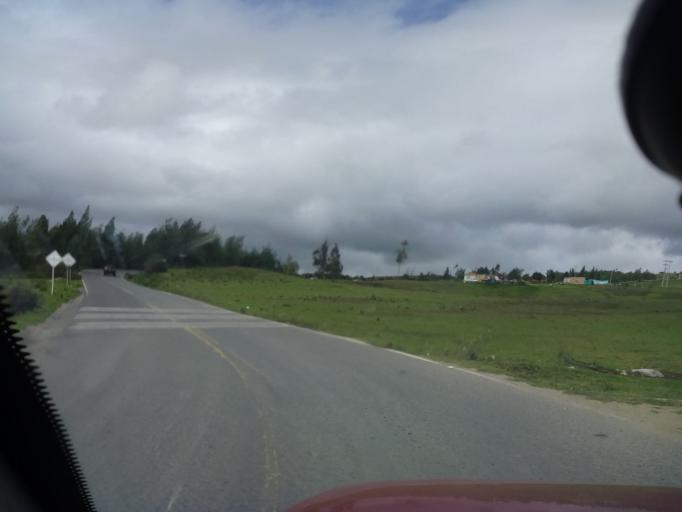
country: CO
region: Boyaca
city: Combita
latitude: 5.6323
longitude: -73.3297
